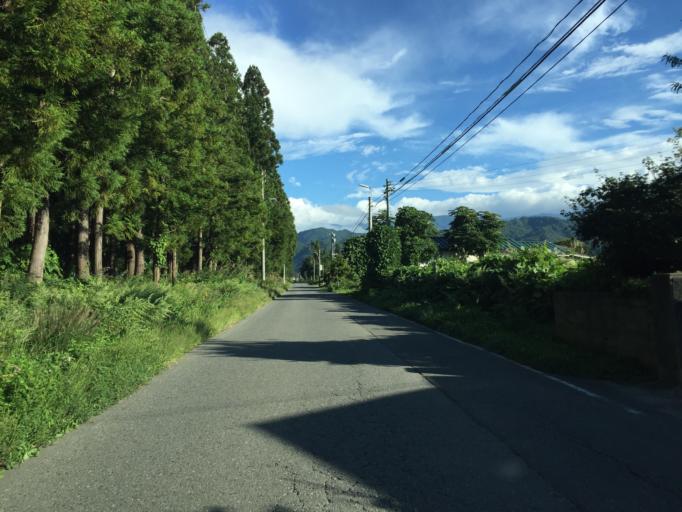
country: JP
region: Yamagata
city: Yonezawa
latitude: 37.8776
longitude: 140.1372
